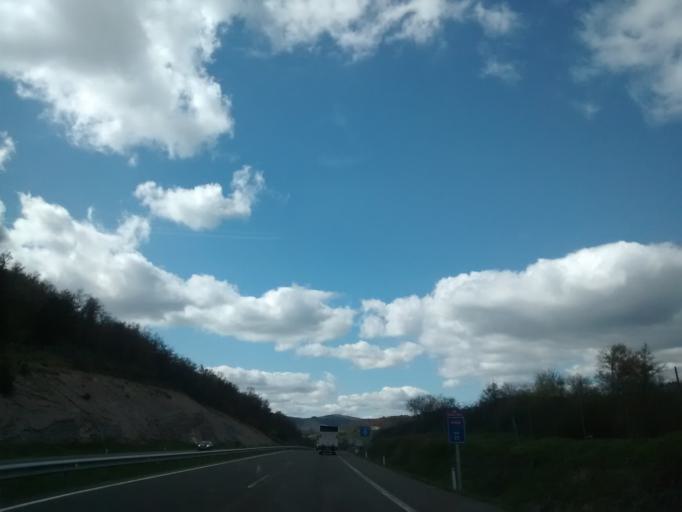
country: ES
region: Basque Country
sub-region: Provincia de Alava
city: Murguia
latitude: 42.9497
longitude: -2.7959
